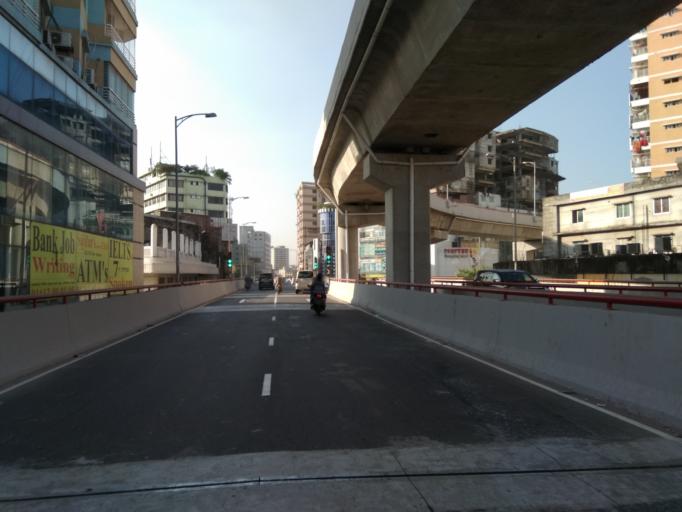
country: BD
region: Dhaka
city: Paltan
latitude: 23.7451
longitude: 90.4128
